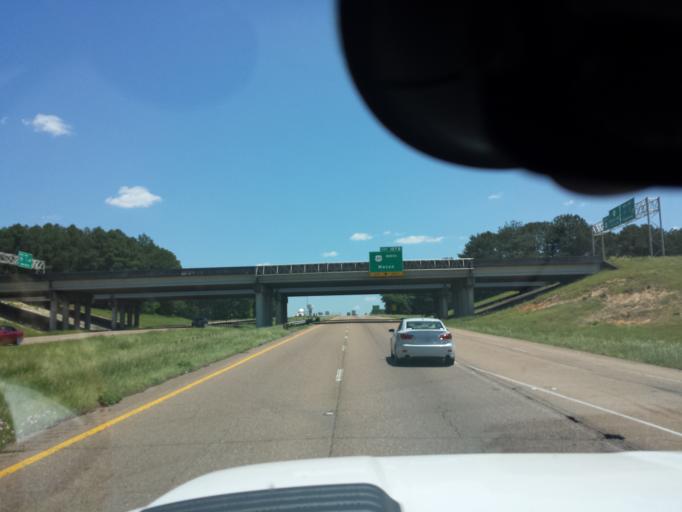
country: US
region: Mississippi
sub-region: Lauderdale County
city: Marion
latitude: 32.3830
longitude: -88.6377
